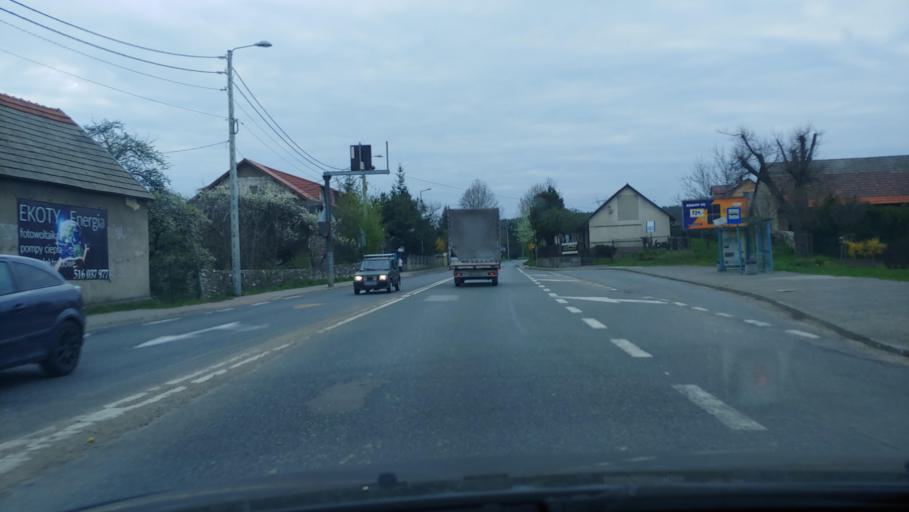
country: PL
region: Silesian Voivodeship
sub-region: Jaworzno
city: Jaworzno
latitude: 50.1637
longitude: 19.3067
